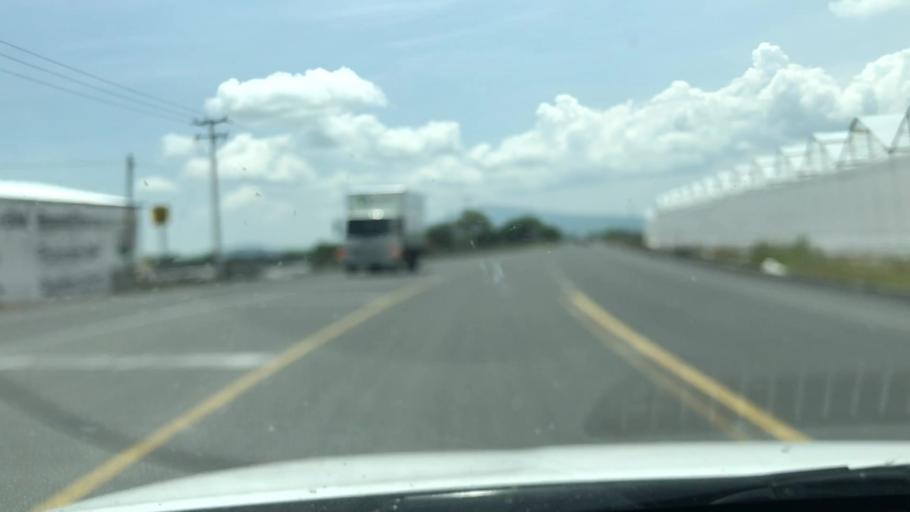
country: MX
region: Michoacan
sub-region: Yurecuaro
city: Yurecuaro
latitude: 20.3194
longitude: -102.3006
